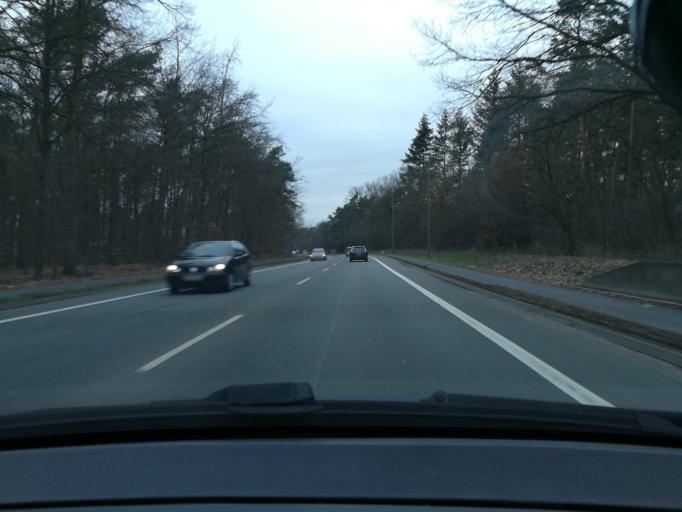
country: DE
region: North Rhine-Westphalia
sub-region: Regierungsbezirk Detmold
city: Oerlinghausen
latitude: 51.9402
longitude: 8.5905
